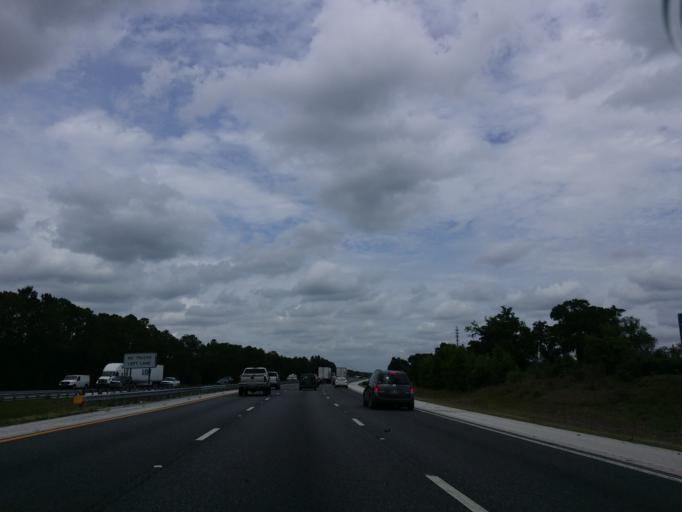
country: US
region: Florida
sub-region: Marion County
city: Ocala
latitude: 29.0799
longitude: -82.1848
